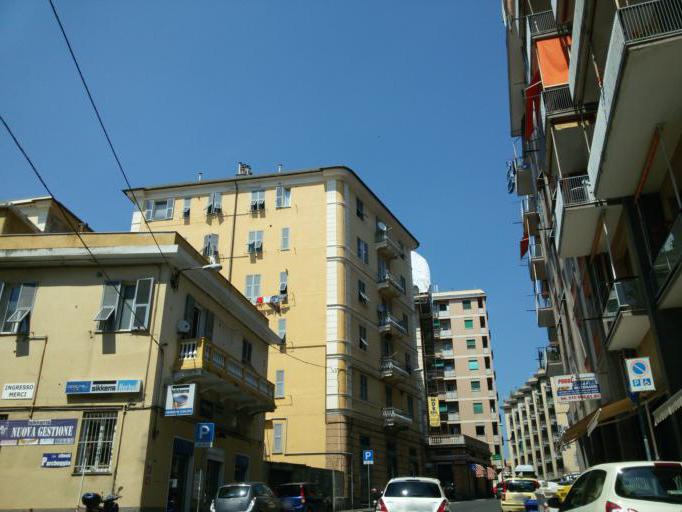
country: IT
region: Liguria
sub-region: Provincia di Genova
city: San Teodoro
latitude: 44.4257
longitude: 8.8555
